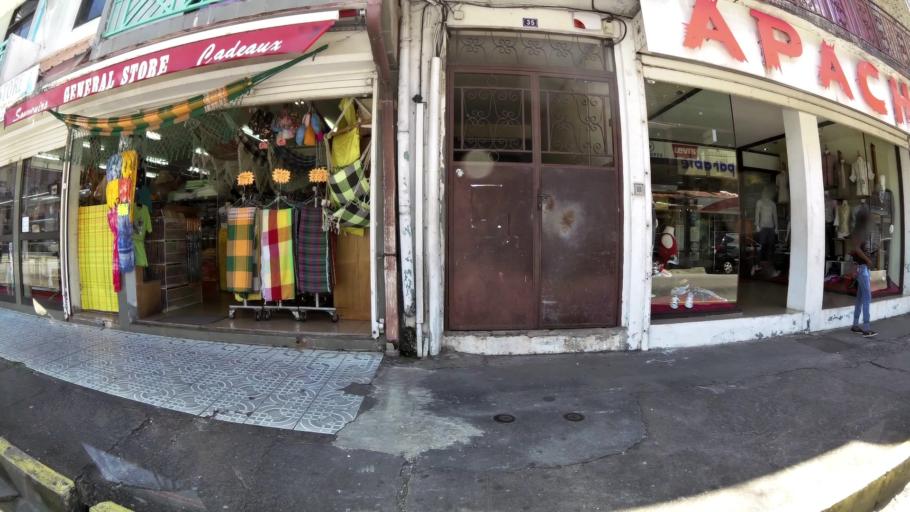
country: GF
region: Guyane
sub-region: Guyane
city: Cayenne
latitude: 4.9392
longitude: -52.3304
